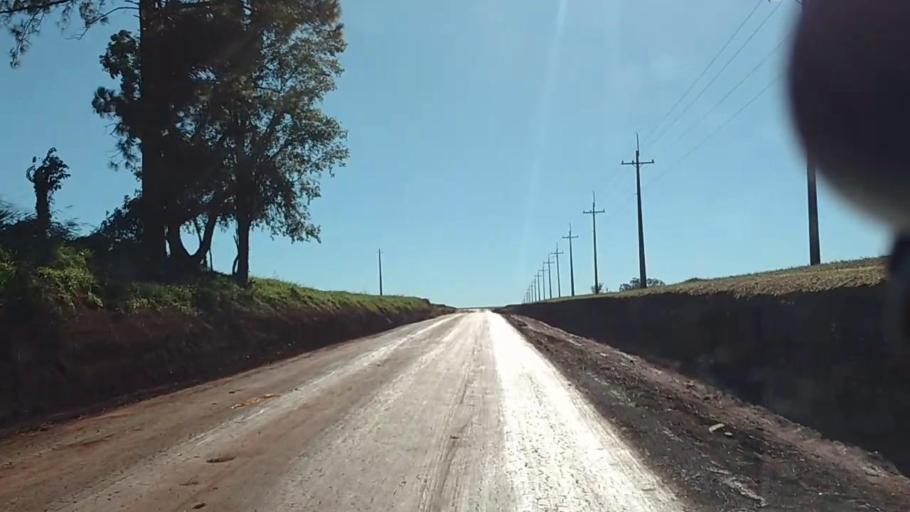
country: PY
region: Alto Parana
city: Naranjal
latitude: -25.9717
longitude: -55.2361
